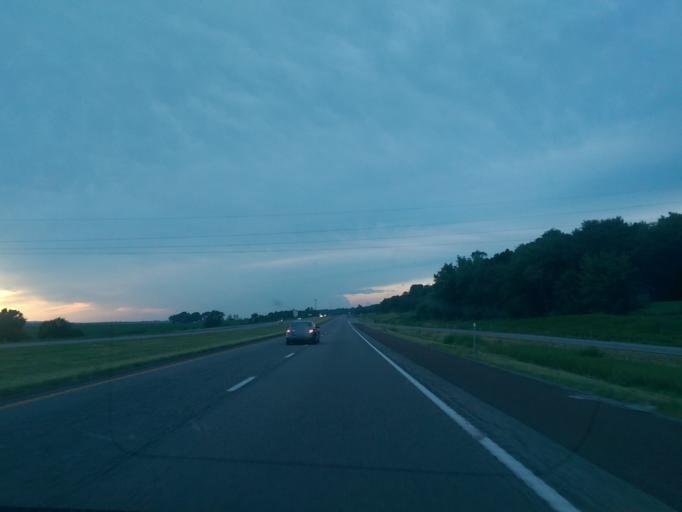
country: US
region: Missouri
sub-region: Holt County
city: Mound City
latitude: 40.1950
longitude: -95.3616
